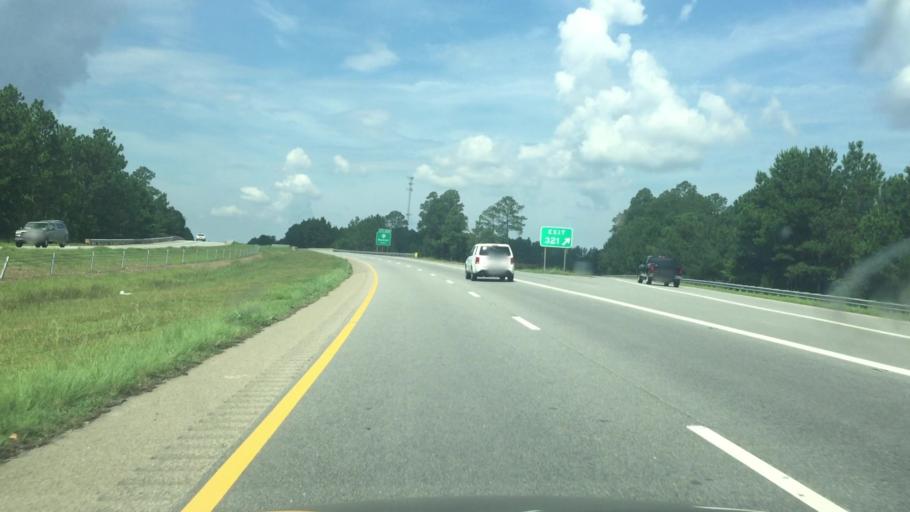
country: US
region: North Carolina
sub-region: Richmond County
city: Hamlet
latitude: 34.8689
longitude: -79.6467
